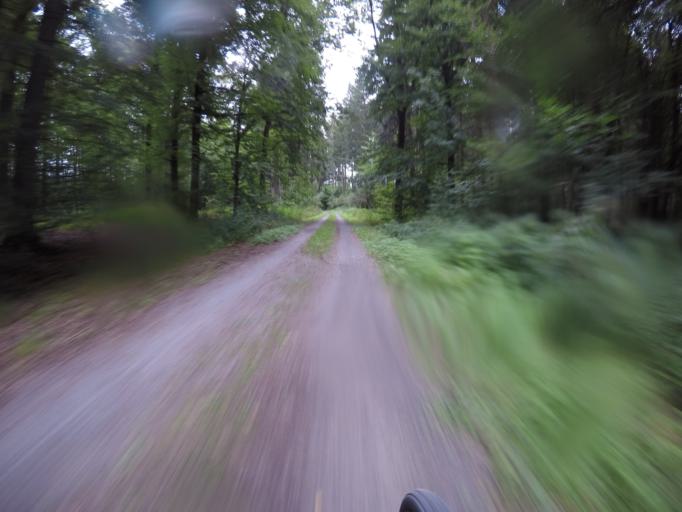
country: DE
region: Baden-Wuerttemberg
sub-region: Regierungsbezirk Stuttgart
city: Schonaich
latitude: 48.6903
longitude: 9.0508
